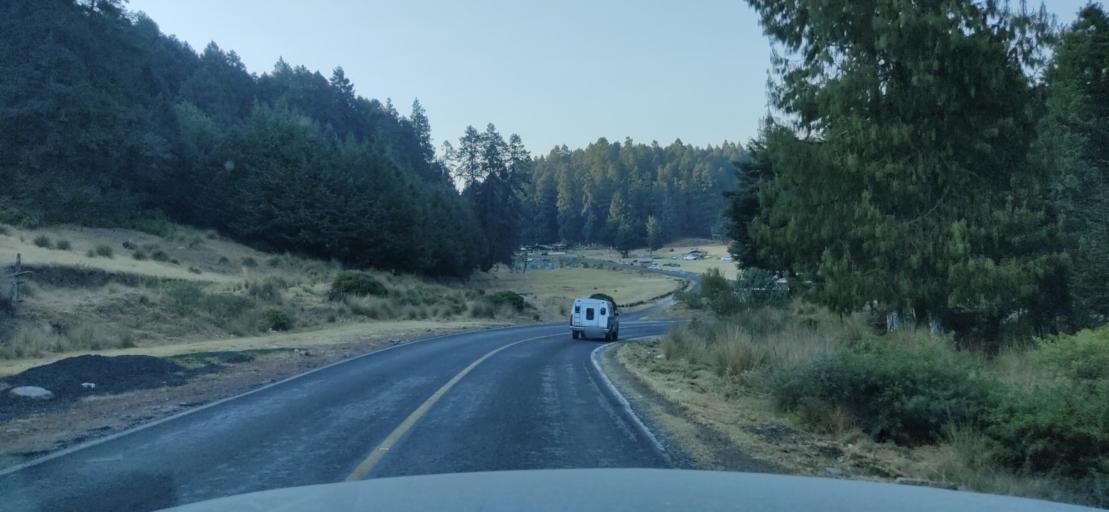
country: MX
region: Mexico
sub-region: Ocoyoacac
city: San Jeronimo Acazulco
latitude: 19.2793
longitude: -99.3812
